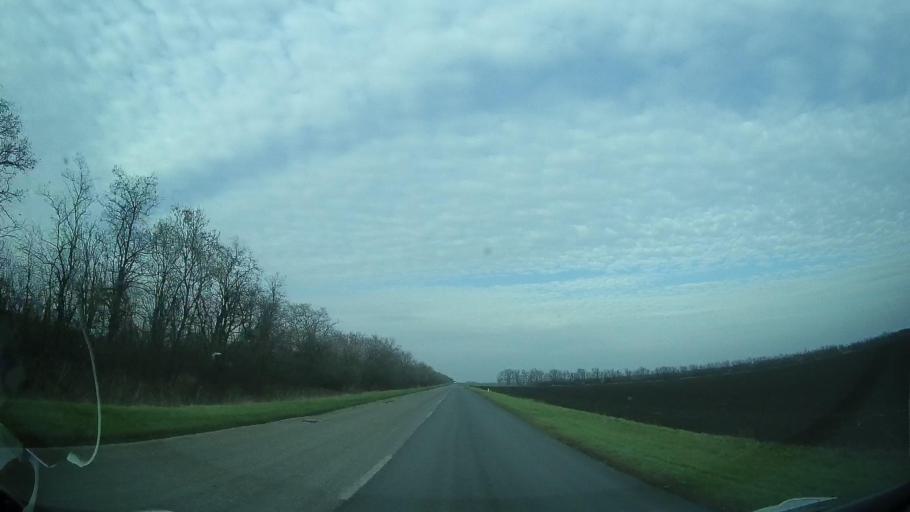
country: RU
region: Rostov
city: Zernograd
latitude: 46.9366
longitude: 40.3665
